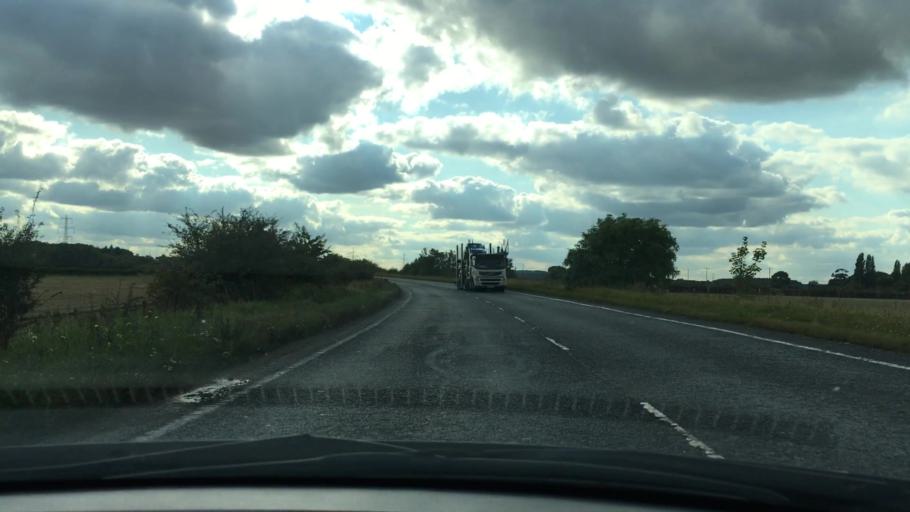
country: GB
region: England
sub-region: North East Lincolnshire
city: Immingham
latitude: 53.6024
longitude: -0.1908
